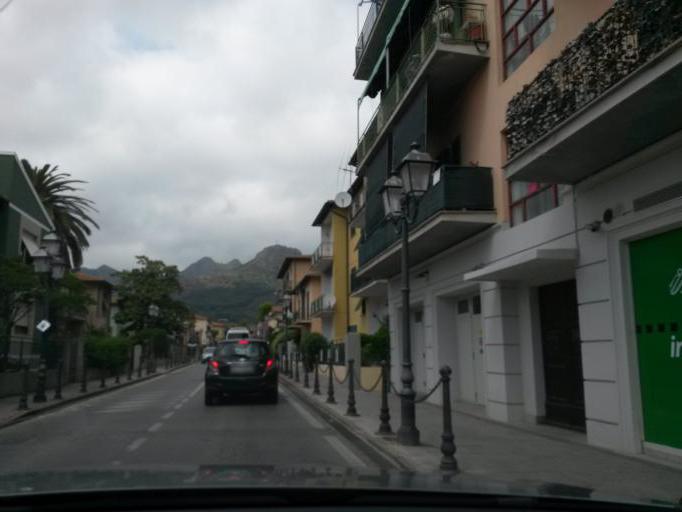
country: IT
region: Tuscany
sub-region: Provincia di Livorno
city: Porto Azzurro
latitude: 42.7658
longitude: 10.3953
